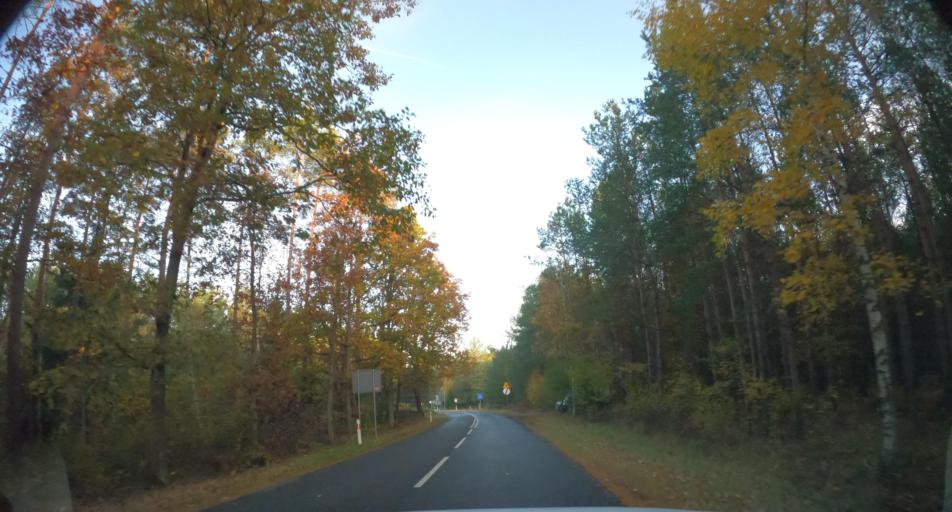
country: PL
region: West Pomeranian Voivodeship
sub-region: Powiat policki
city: Nowe Warpno
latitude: 53.6087
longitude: 14.3165
